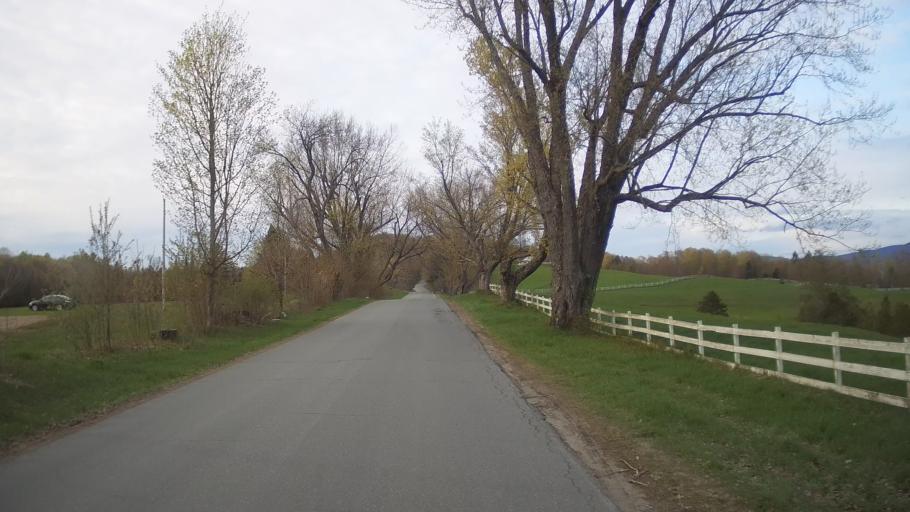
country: US
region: Vermont
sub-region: Caledonia County
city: Lyndonville
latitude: 44.5905
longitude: -71.9597
